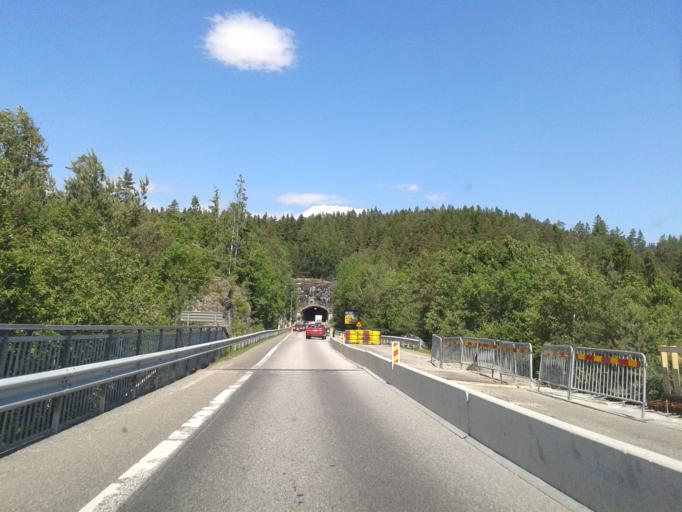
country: SE
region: Vaestra Goetaland
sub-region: Orust
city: Henan
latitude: 58.2955
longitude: 11.7023
